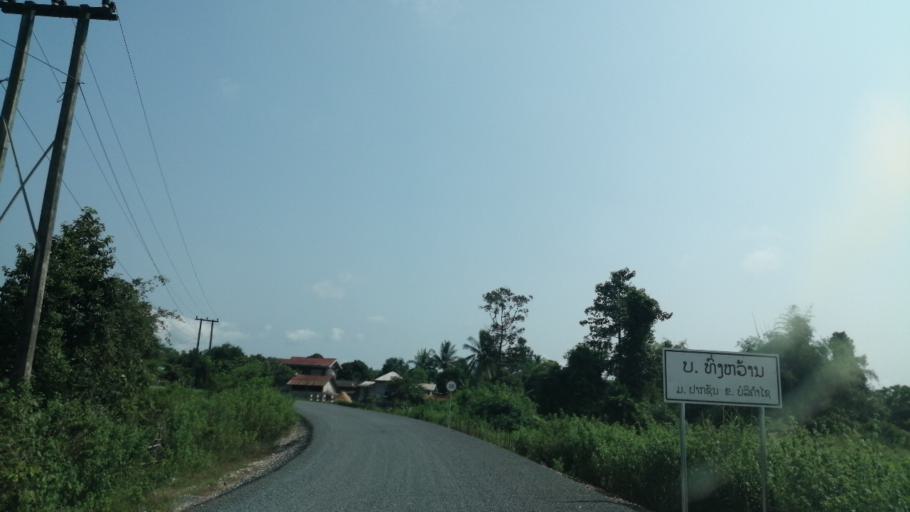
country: TH
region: Changwat Bueng Kan
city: Bung Khla
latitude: 18.3954
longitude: 103.8475
